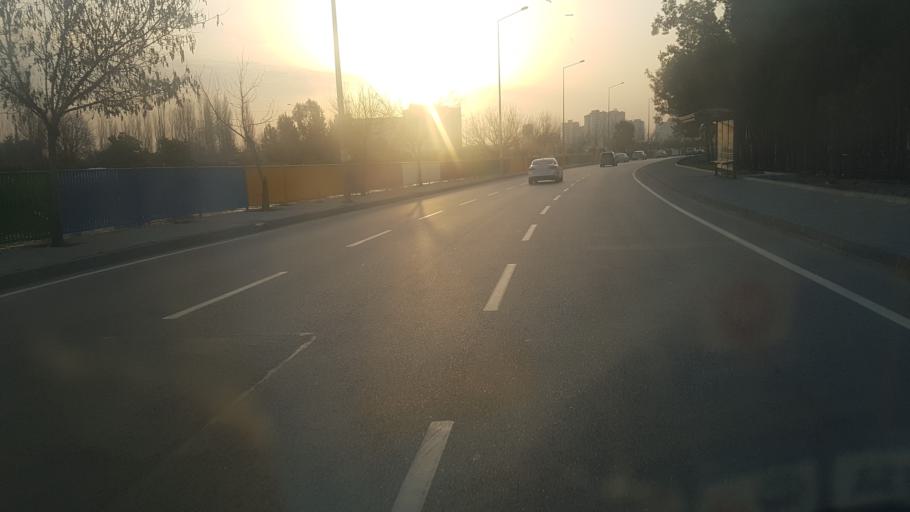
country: TR
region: Adana
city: Adana
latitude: 37.0124
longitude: 35.3491
